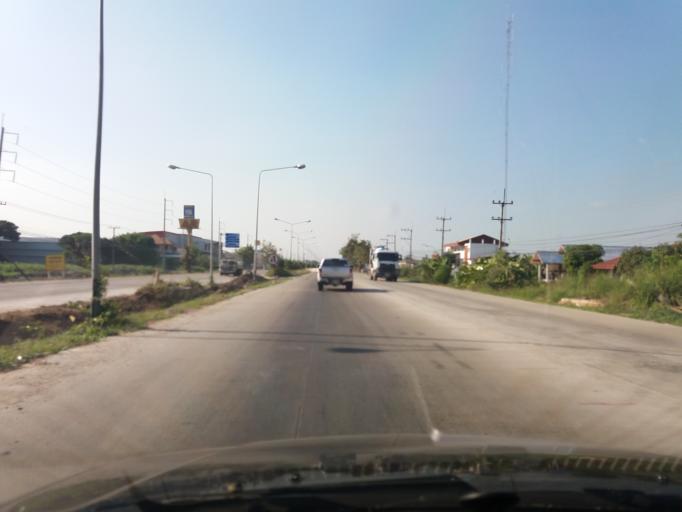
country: TH
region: Nakhon Sawan
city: Kao Liao
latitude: 15.7582
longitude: 99.9969
